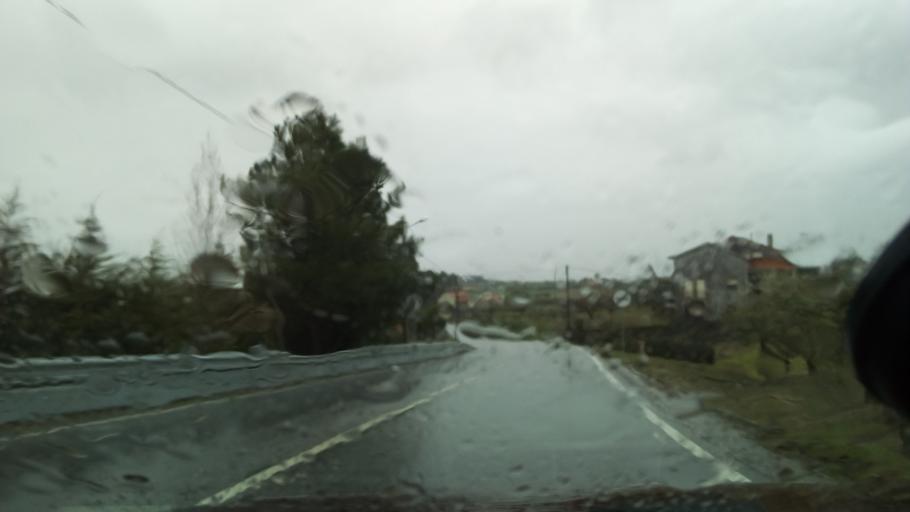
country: PT
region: Guarda
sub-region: Manteigas
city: Manteigas
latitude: 40.5063
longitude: -7.5883
